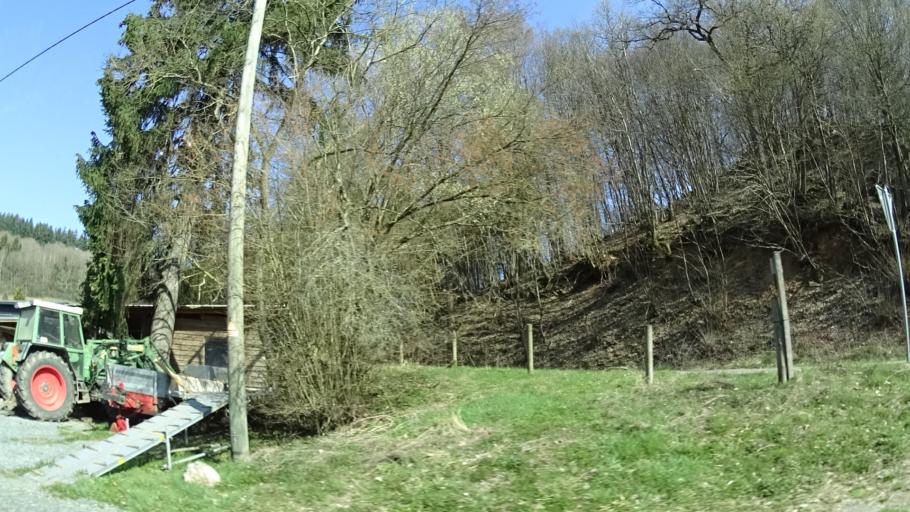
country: DE
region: Rheinland-Pfalz
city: Niederhambach
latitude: 49.6845
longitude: 7.1904
